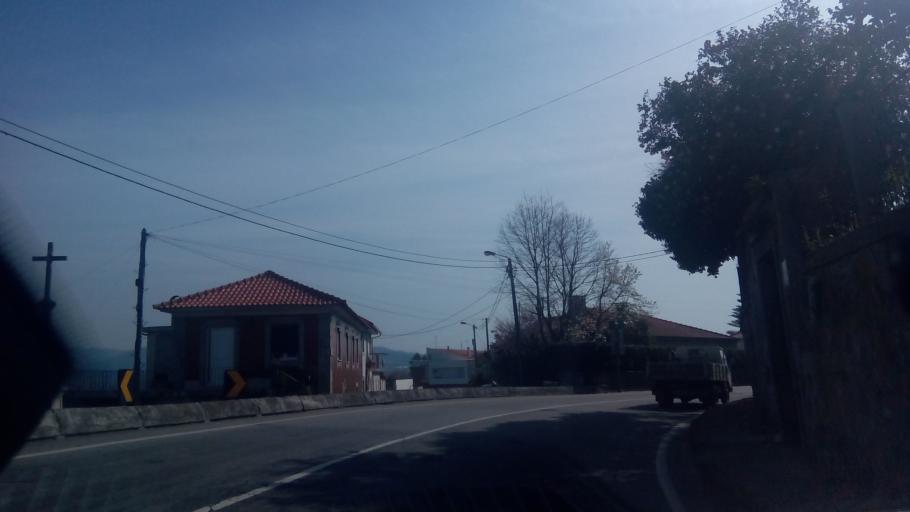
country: PT
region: Viana do Castelo
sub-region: Viana do Castelo
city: Darque
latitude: 41.6822
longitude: -8.7861
